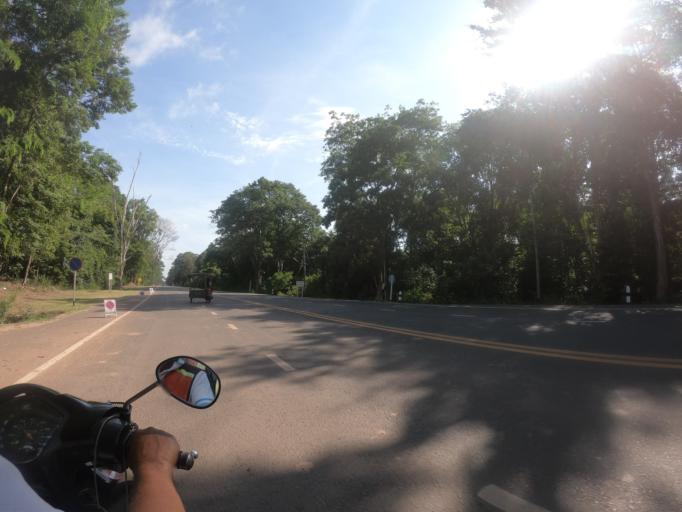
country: TH
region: Surin
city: Kap Choeng
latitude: 14.4372
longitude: 103.7007
